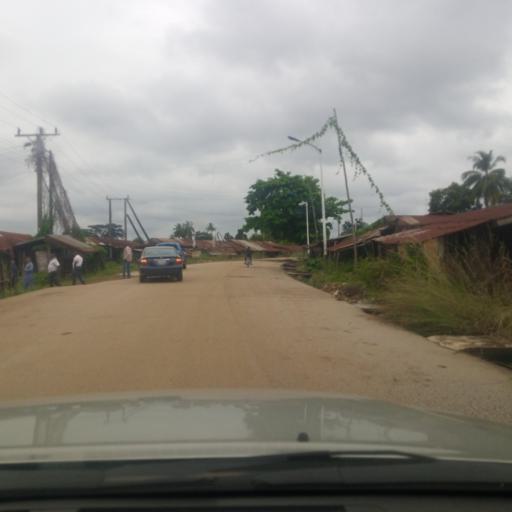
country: NG
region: Ebonyi
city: Effium
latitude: 6.6291
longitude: 8.0550
